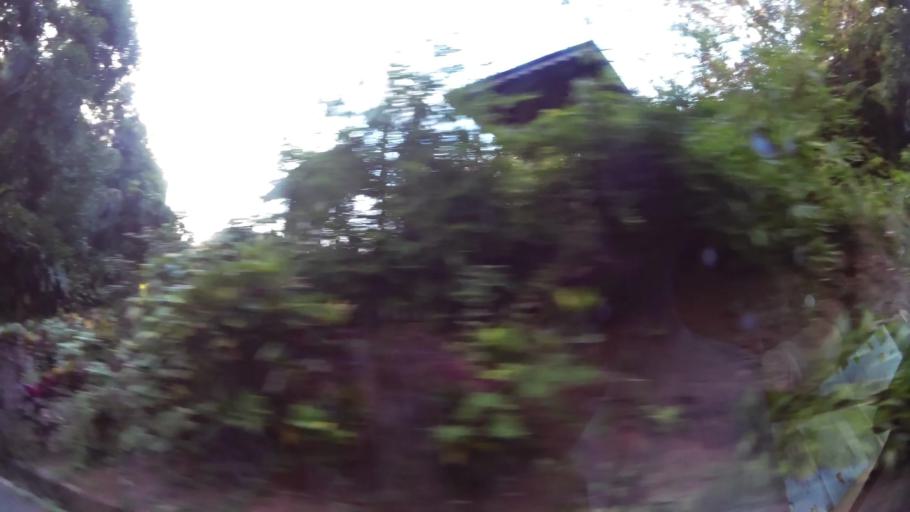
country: DM
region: Saint John
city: Portsmouth
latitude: 15.5800
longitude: -61.4229
